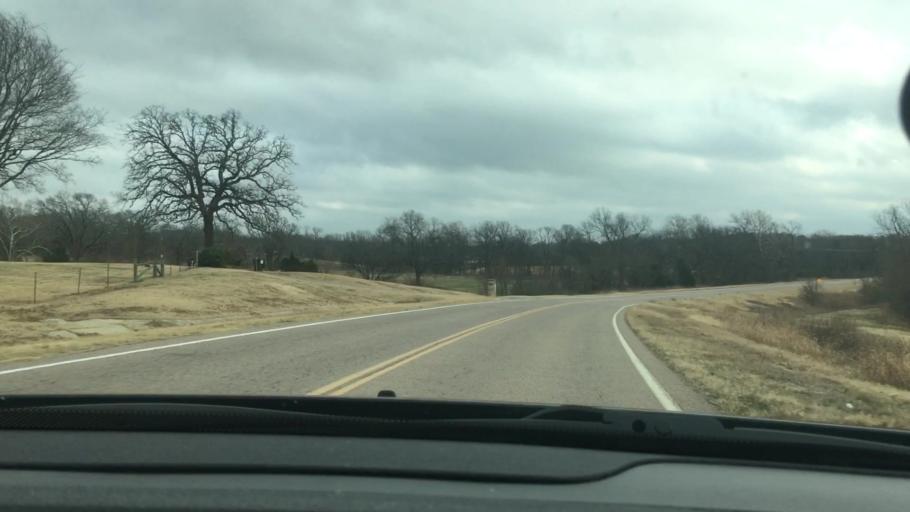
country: US
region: Oklahoma
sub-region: Bryan County
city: Durant
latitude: 34.0859
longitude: -96.3857
